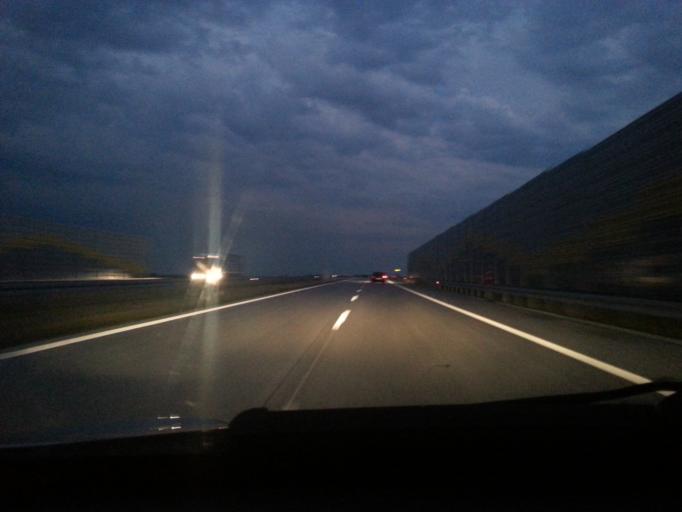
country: PL
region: Lodz Voivodeship
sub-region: Powiat sieradzki
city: Brzeznio
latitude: 51.4731
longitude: 18.6664
